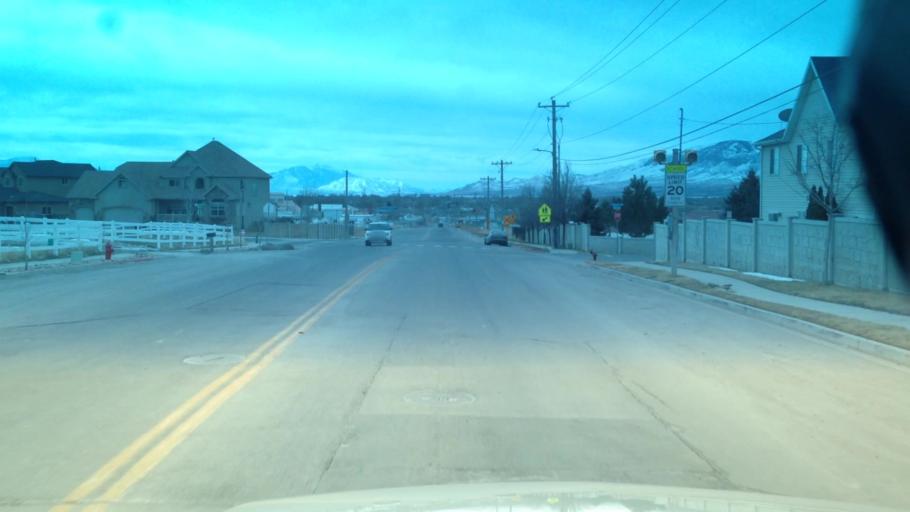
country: US
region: Utah
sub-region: Utah County
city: Lehi
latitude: 40.4236
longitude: -111.8688
